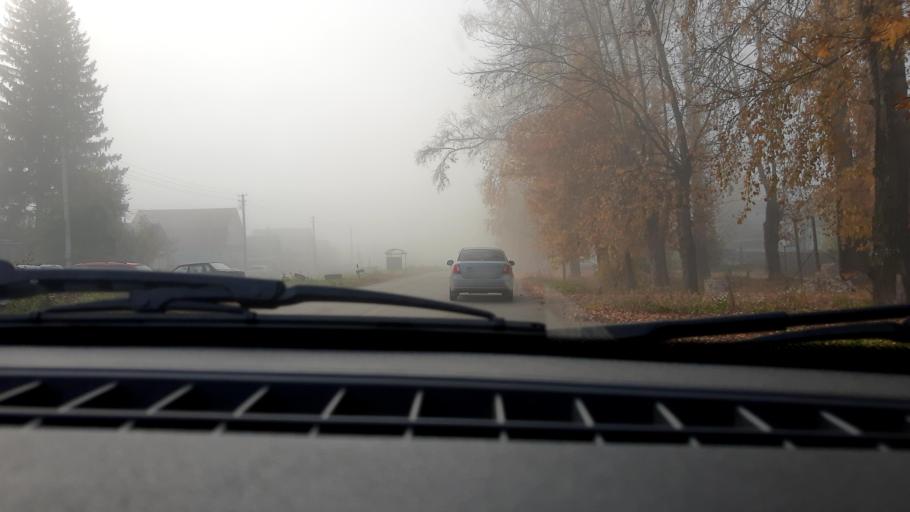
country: RU
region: Bashkortostan
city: Mikhaylovka
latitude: 54.7669
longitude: 55.8971
